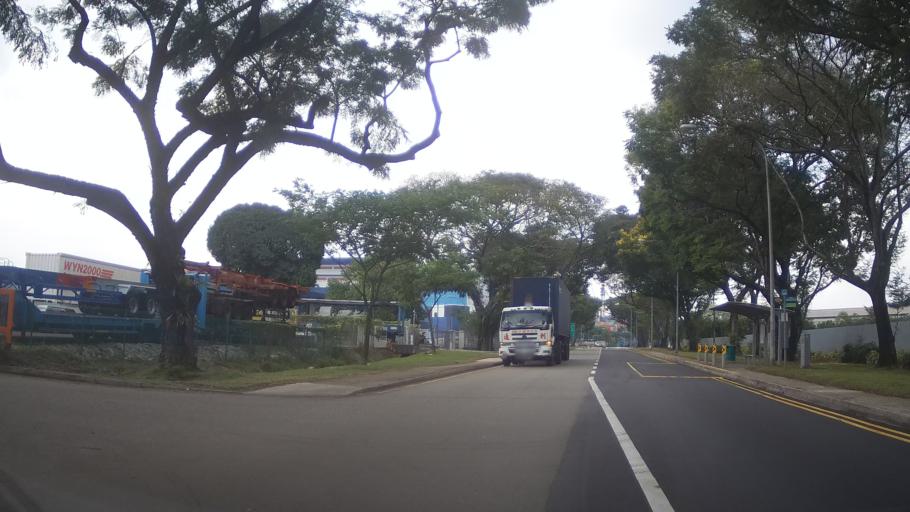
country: SG
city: Singapore
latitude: 1.3061
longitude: 103.6790
